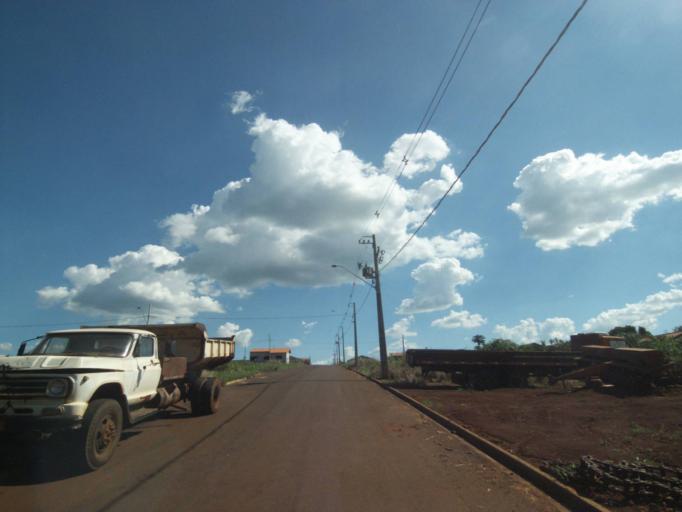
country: BR
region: Parana
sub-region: Sertanopolis
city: Sertanopolis
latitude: -23.0347
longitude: -50.8111
